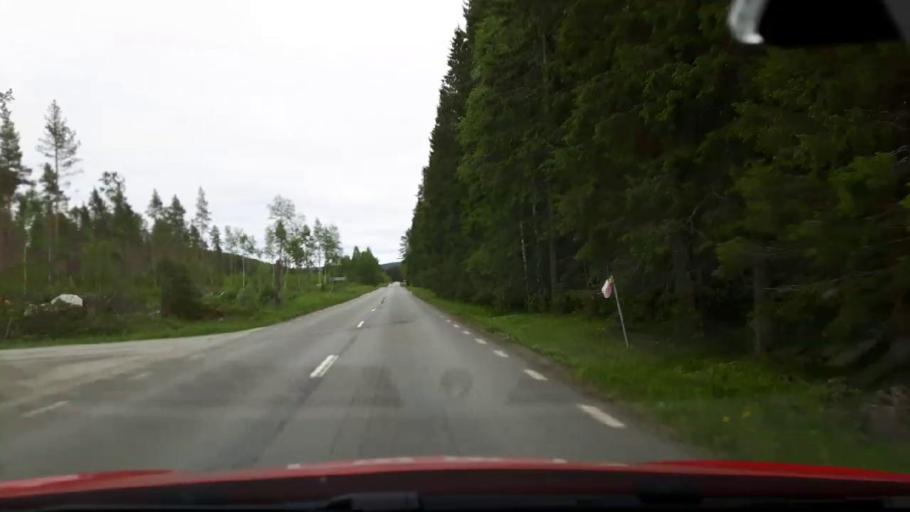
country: SE
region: Jaemtland
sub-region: Stroemsunds Kommun
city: Stroemsund
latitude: 63.4420
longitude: 15.4816
